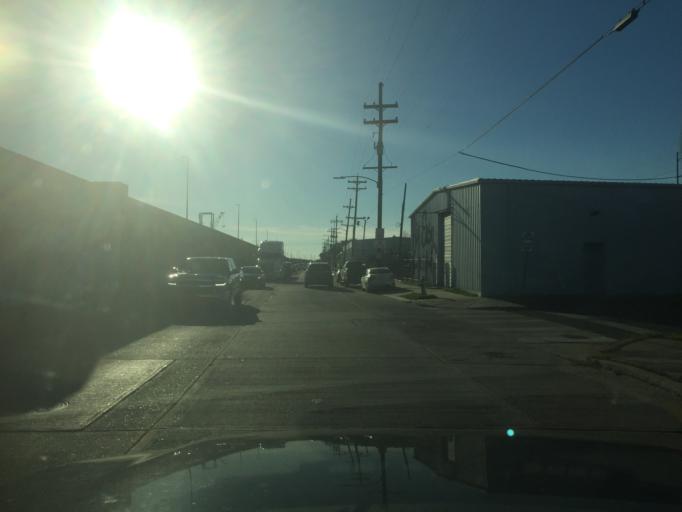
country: US
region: Louisiana
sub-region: Jefferson Parish
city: Harvey
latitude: 29.9219
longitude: -90.0745
